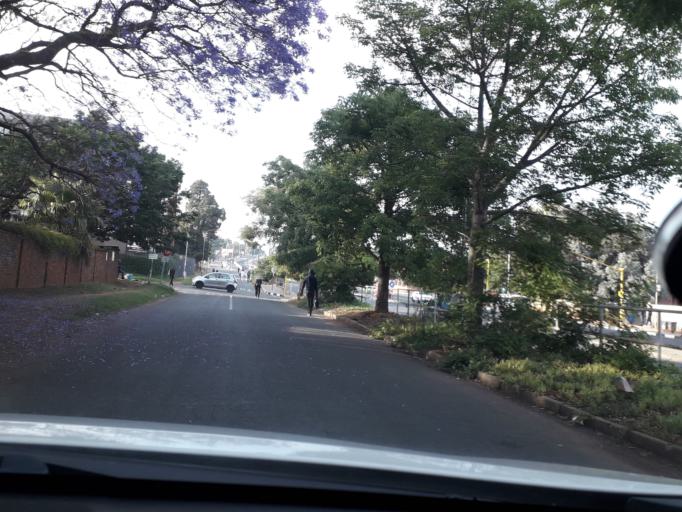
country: ZA
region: Gauteng
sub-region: City of Johannesburg Metropolitan Municipality
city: Johannesburg
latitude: -26.1340
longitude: 28.0861
